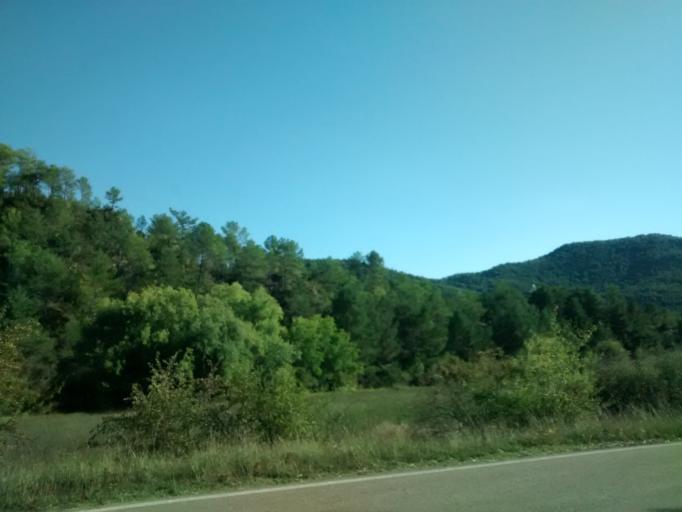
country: ES
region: Aragon
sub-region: Provincia de Huesca
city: Santa Cruz de la Seros
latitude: 42.4302
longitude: -0.6247
